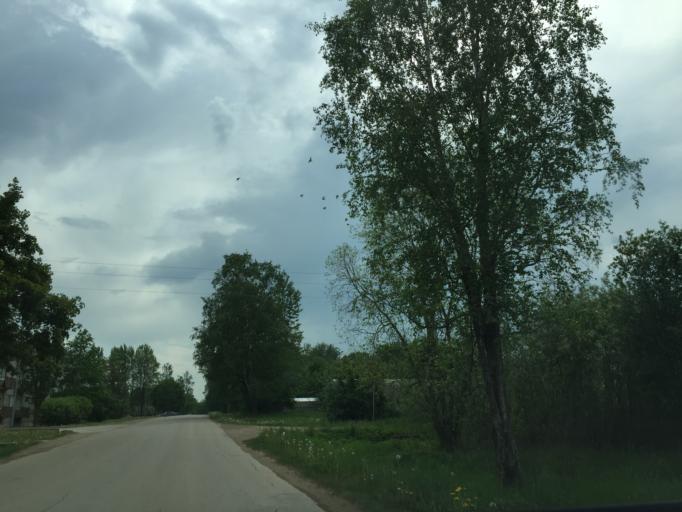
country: LV
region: Livani
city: Livani
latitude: 56.5395
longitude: 26.2434
